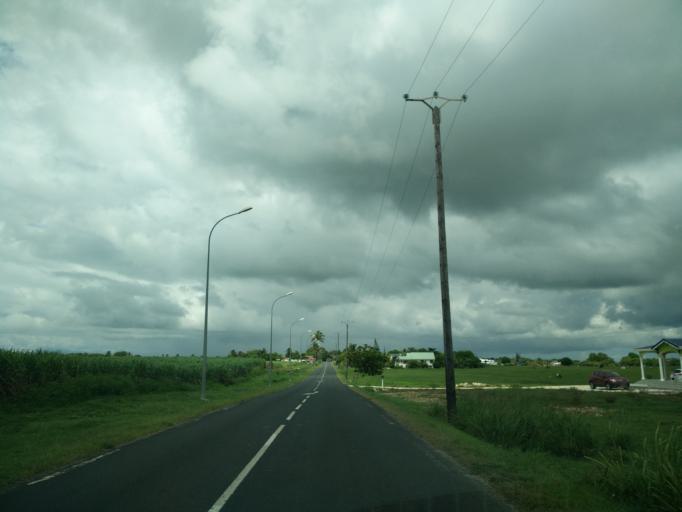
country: GP
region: Guadeloupe
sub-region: Guadeloupe
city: Saint-Francois
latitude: 16.2670
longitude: -61.3302
